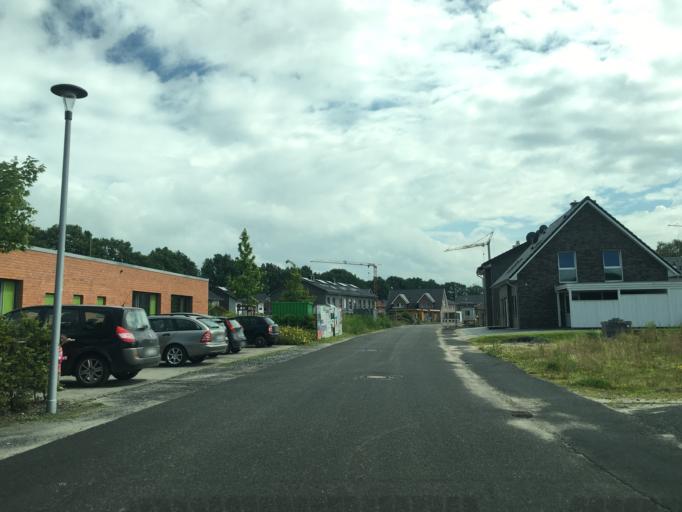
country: DE
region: North Rhine-Westphalia
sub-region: Regierungsbezirk Munster
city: Greven
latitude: 52.0380
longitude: 7.6121
